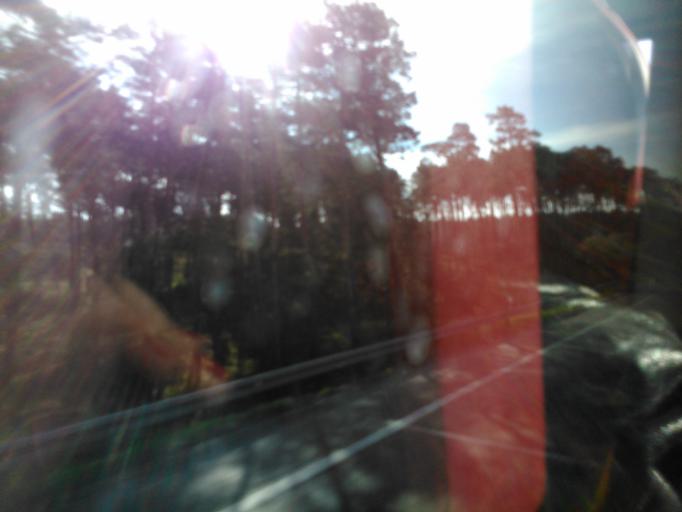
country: PL
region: Kujawsko-Pomorskie
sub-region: Powiat aleksandrowski
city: Aleksandrow Kujawski
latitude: 52.9286
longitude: 18.7074
